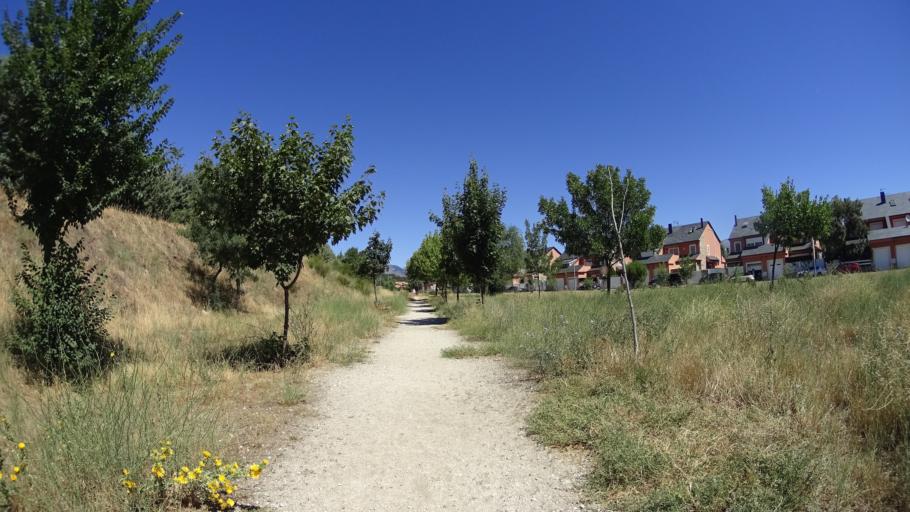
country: ES
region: Madrid
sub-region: Provincia de Madrid
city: Alpedrete
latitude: 40.6450
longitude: -4.0253
